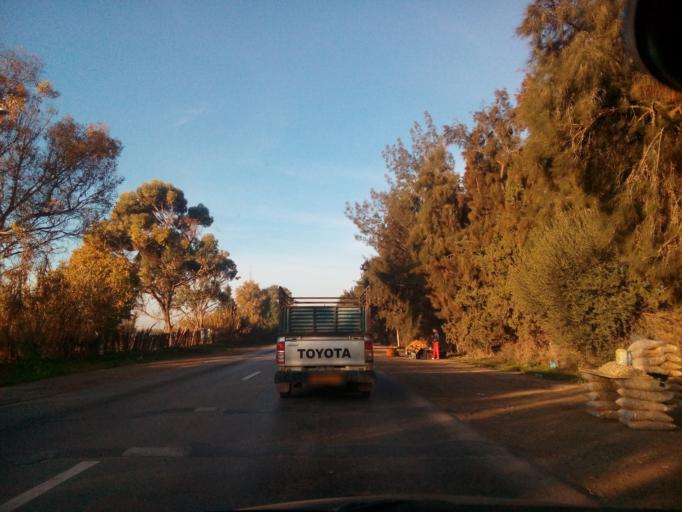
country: DZ
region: Relizane
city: Relizane
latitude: 35.7246
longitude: 0.3748
